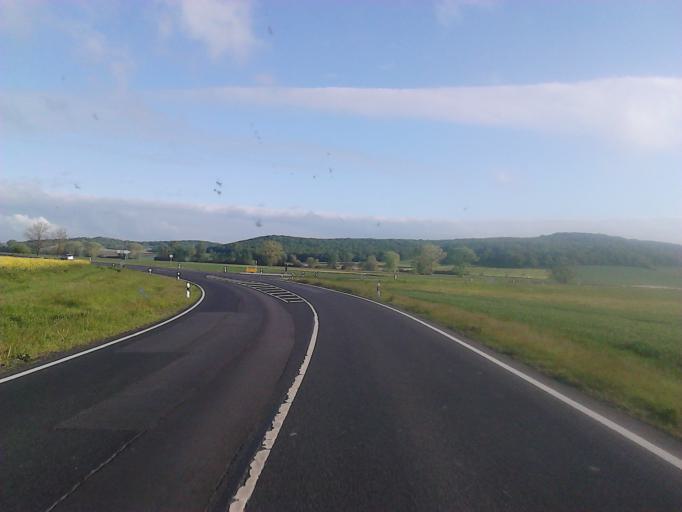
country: DE
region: Bavaria
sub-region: Regierungsbezirk Unterfranken
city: Bundorf
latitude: 50.2751
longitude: 10.5237
